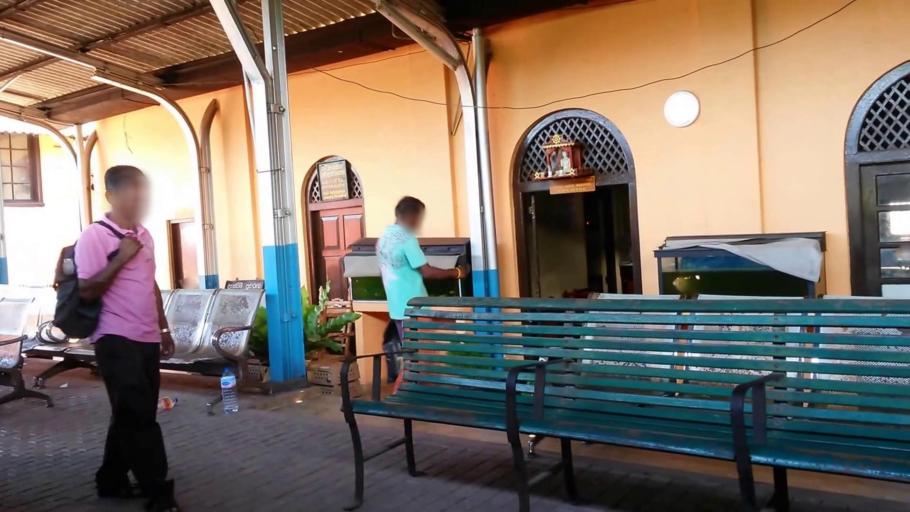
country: LK
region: Southern
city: Hikkaduwa
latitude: 6.1563
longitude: 80.0955
